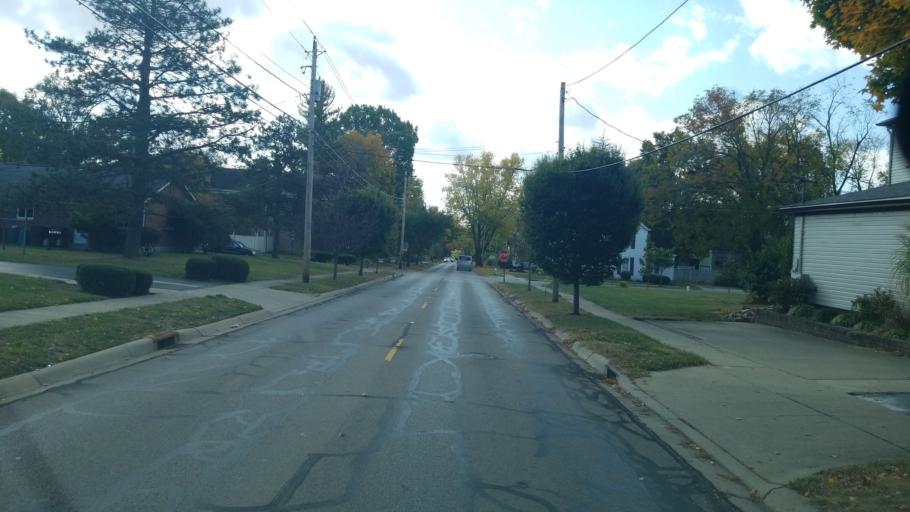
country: US
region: Ohio
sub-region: Warren County
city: Lebanon
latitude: 39.4366
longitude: -84.1987
